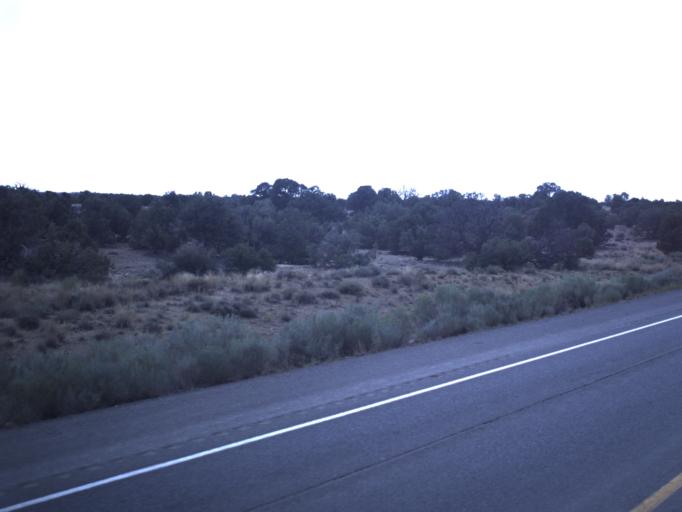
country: US
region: Utah
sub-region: Duchesne County
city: Duchesne
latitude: 40.1651
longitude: -110.4710
